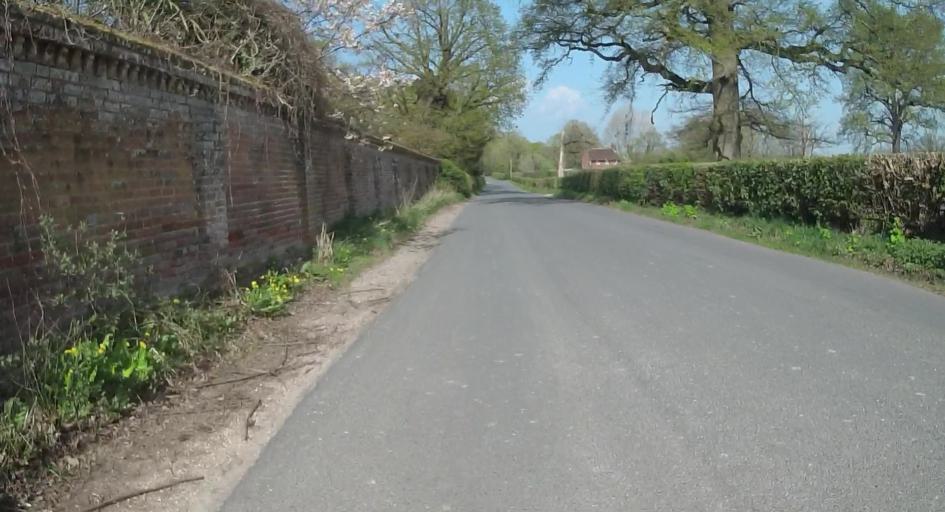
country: GB
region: England
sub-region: Hampshire
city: Basingstoke
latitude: 51.3072
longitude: -1.0865
